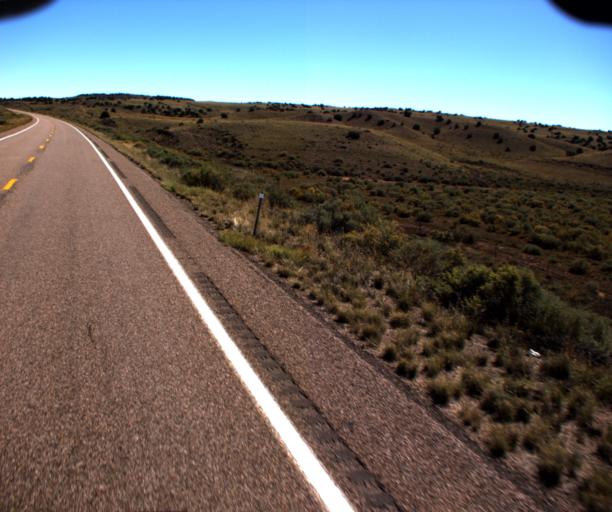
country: US
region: Arizona
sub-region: Apache County
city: Saint Johns
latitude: 34.5849
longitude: -109.5713
